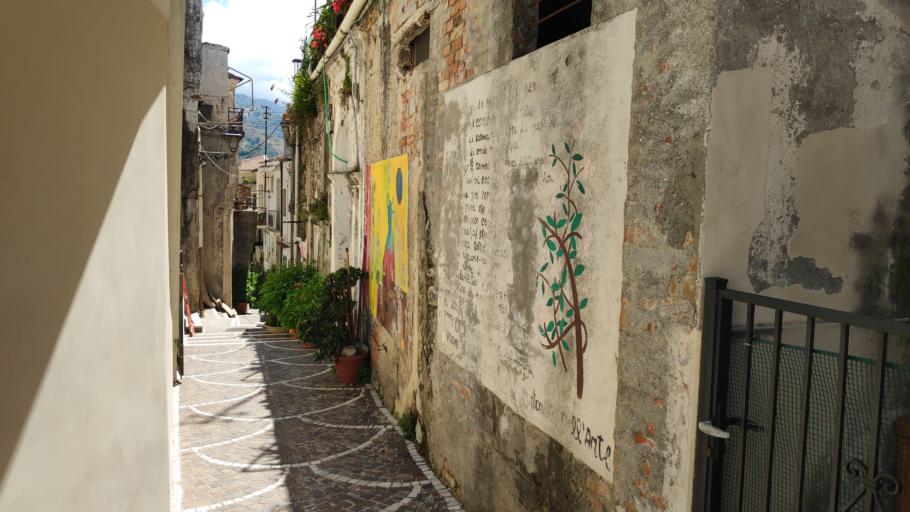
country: IT
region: Calabria
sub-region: Provincia di Cosenza
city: Diamante
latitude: 39.6784
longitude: 15.8174
